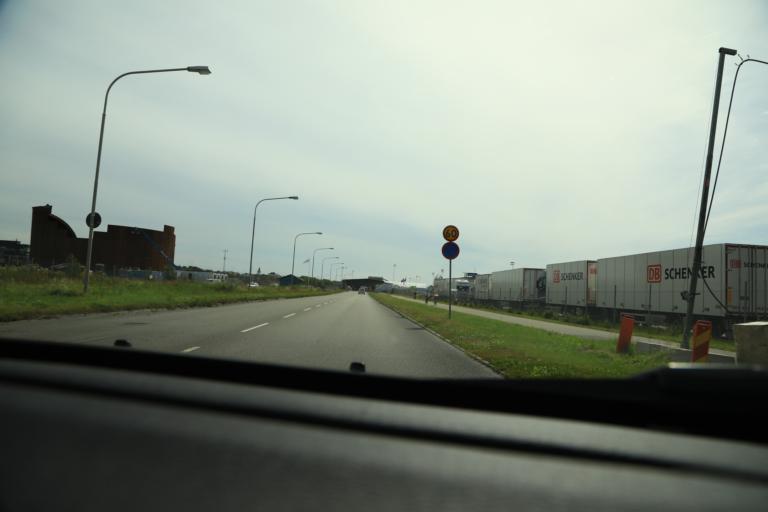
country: SE
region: Halland
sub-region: Varbergs Kommun
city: Varberg
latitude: 57.1182
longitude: 12.2488
